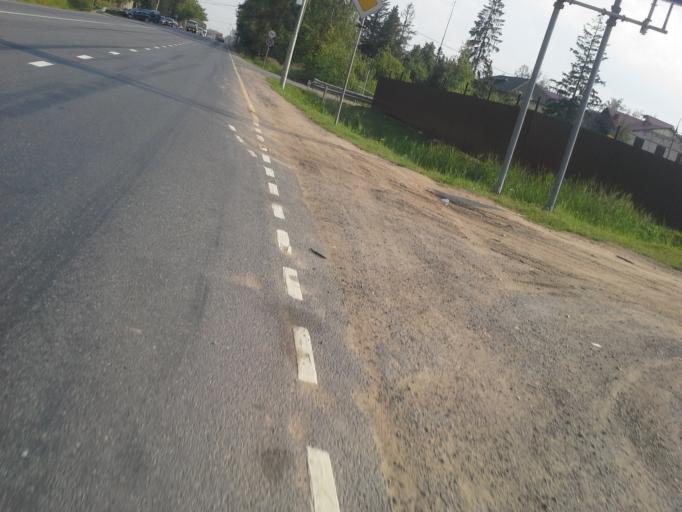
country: RU
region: Moskovskaya
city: Istra
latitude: 55.9065
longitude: 36.9451
